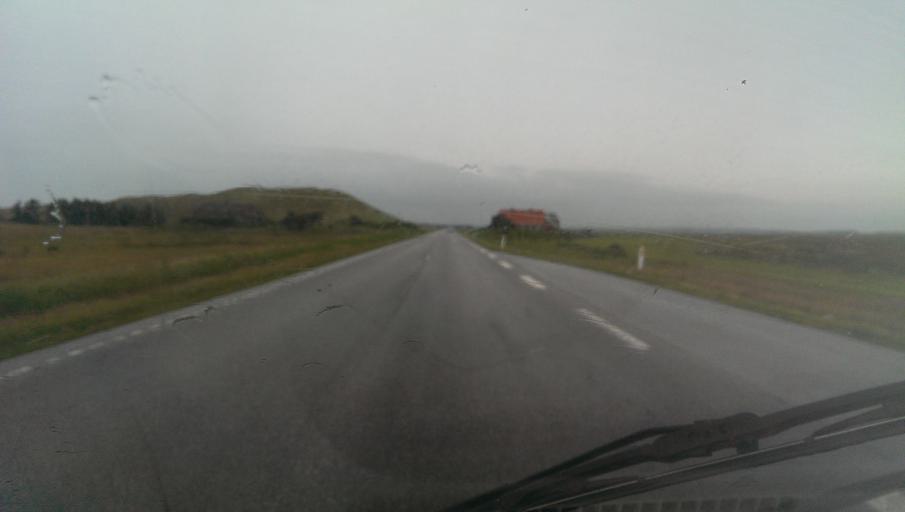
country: DK
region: Central Jutland
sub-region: Ringkobing-Skjern Kommune
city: Ringkobing
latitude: 56.2290
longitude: 8.1396
